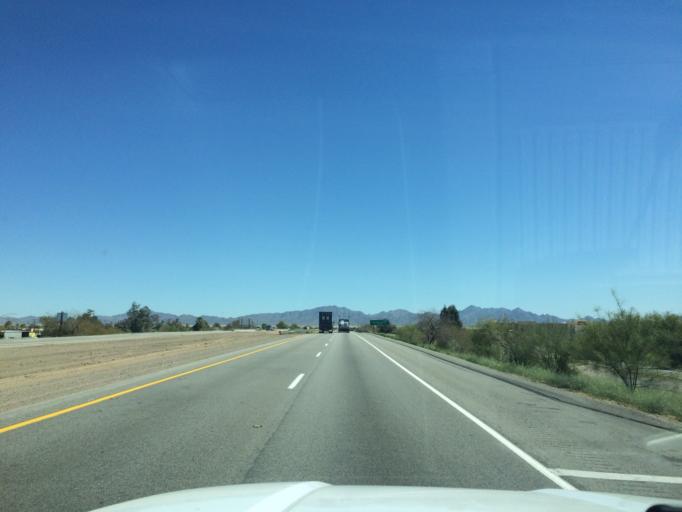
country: US
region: California
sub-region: Riverside County
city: Blythe
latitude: 33.6072
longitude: -114.5733
